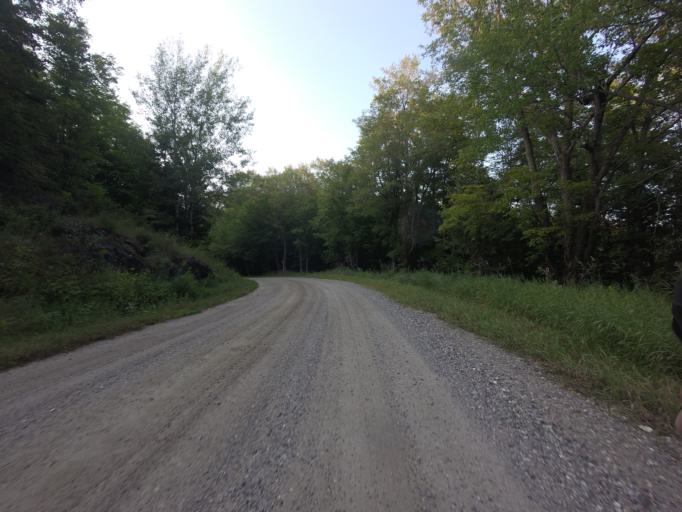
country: CA
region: Ontario
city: Renfrew
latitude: 45.0436
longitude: -76.7425
